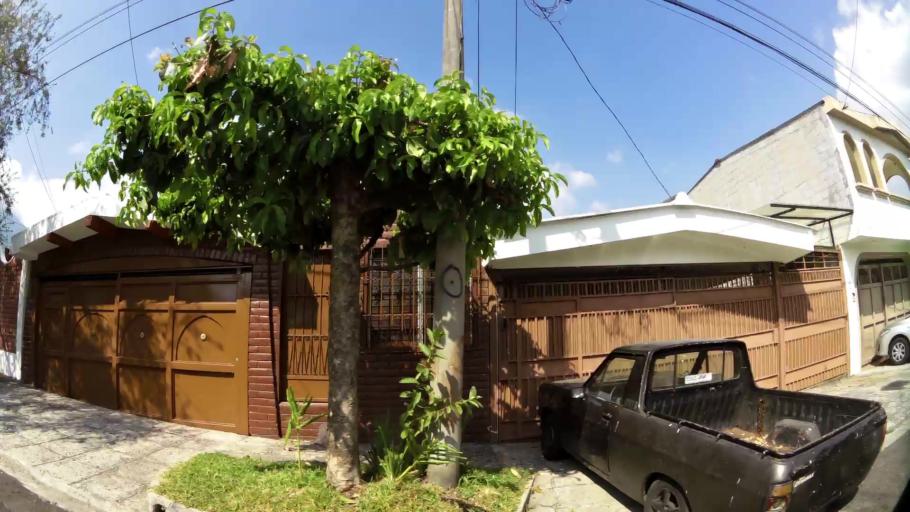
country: SV
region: San Salvador
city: Mejicanos
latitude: 13.7243
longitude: -89.2200
